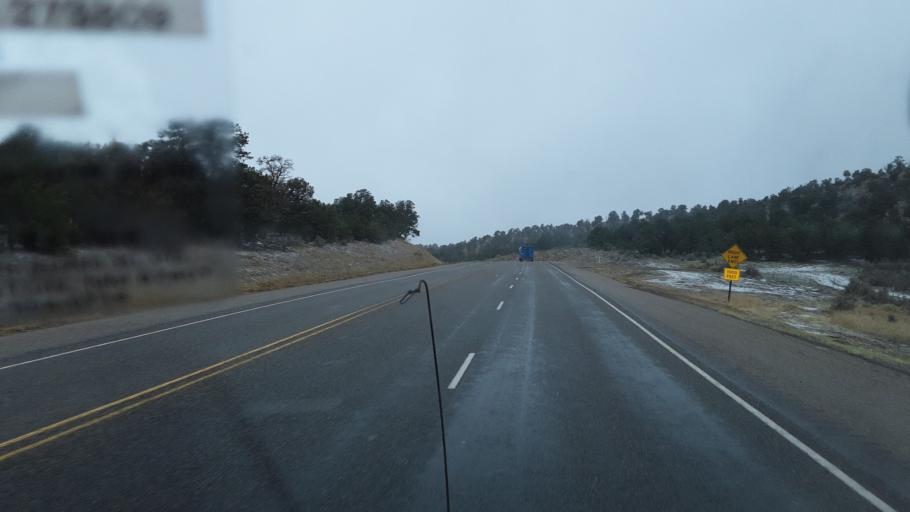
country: US
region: New Mexico
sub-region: Rio Arriba County
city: Tierra Amarilla
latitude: 36.4665
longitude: -106.4798
